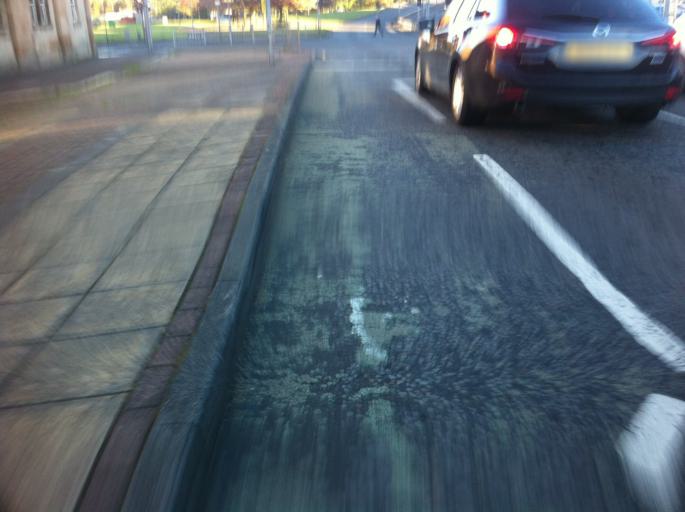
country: GB
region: Scotland
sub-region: Glasgow City
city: Glasgow
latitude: 55.8797
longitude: -4.2337
